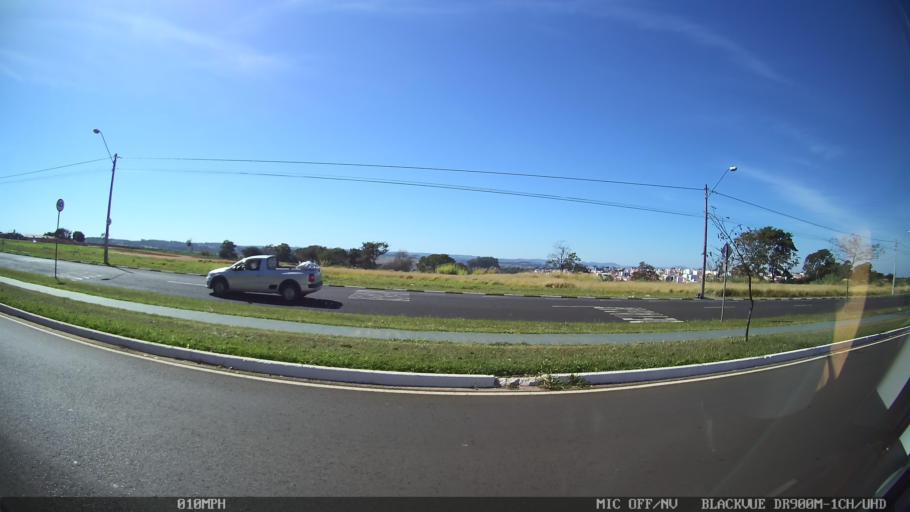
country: BR
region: Sao Paulo
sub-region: Franca
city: Franca
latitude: -20.5618
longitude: -47.3590
